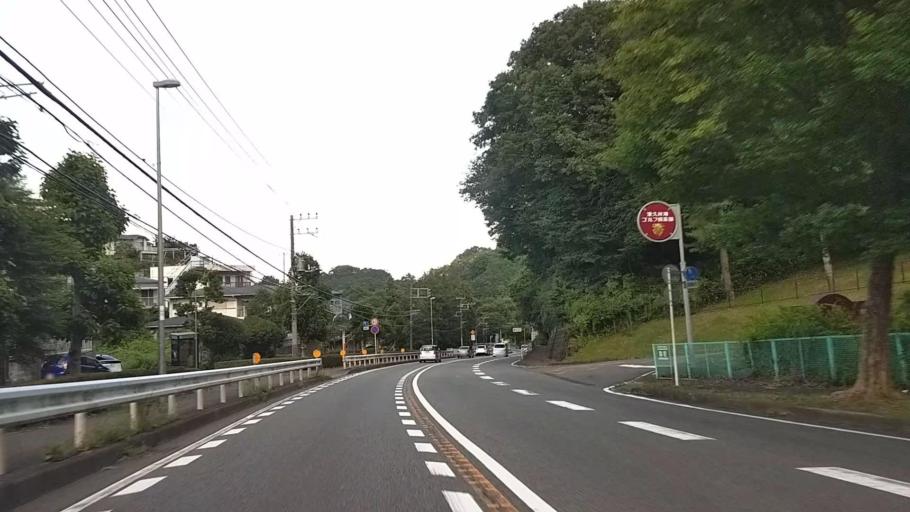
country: JP
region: Tokyo
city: Hachioji
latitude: 35.5878
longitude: 139.2387
